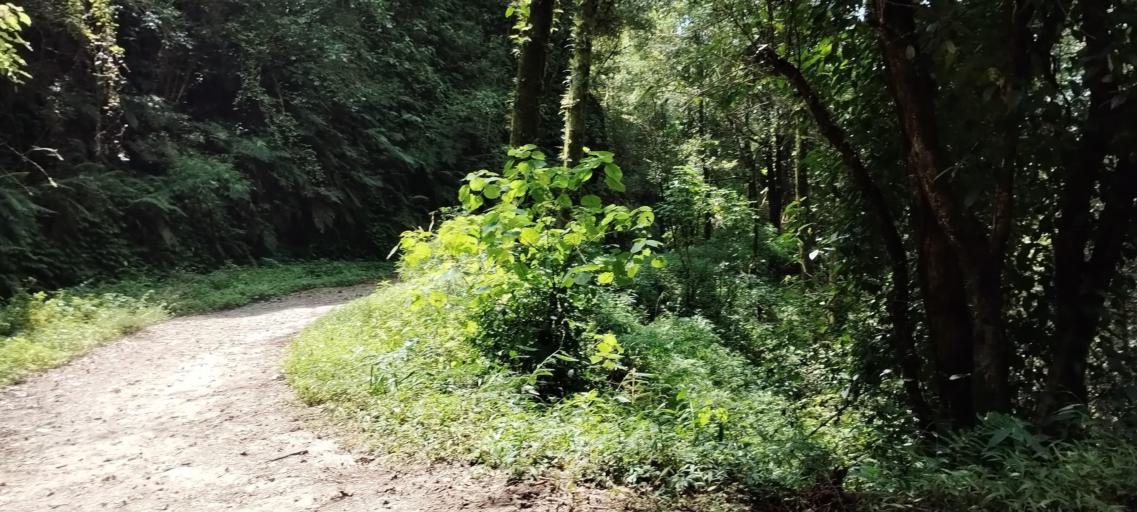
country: NP
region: Central Region
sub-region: Bagmati Zone
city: Kathmandu
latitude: 27.7921
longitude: 85.3752
